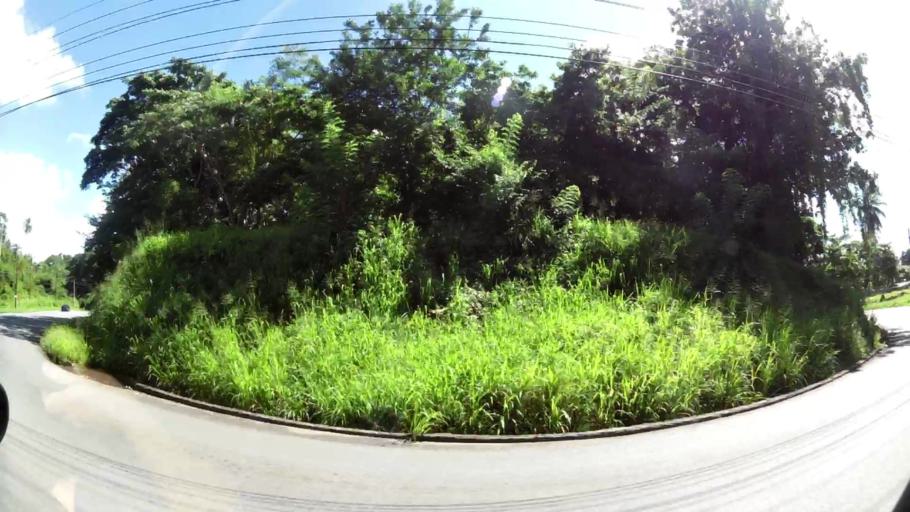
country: TT
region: Tobago
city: Scarborough
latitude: 11.2159
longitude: -60.7764
